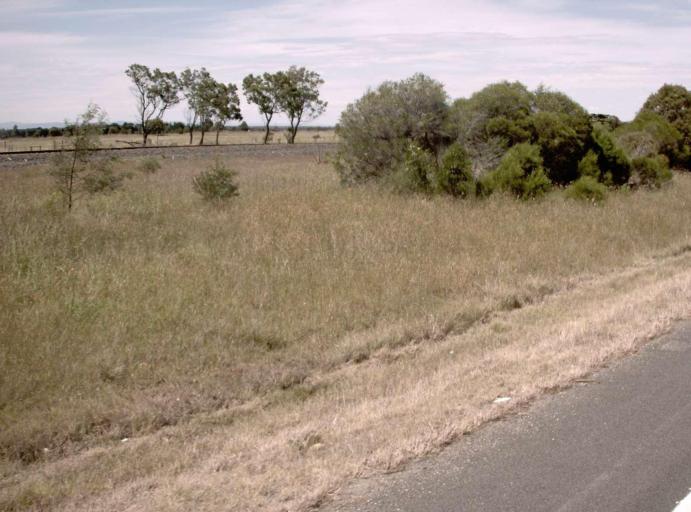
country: AU
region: Victoria
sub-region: Wellington
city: Sale
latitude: -38.1016
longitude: 146.9484
